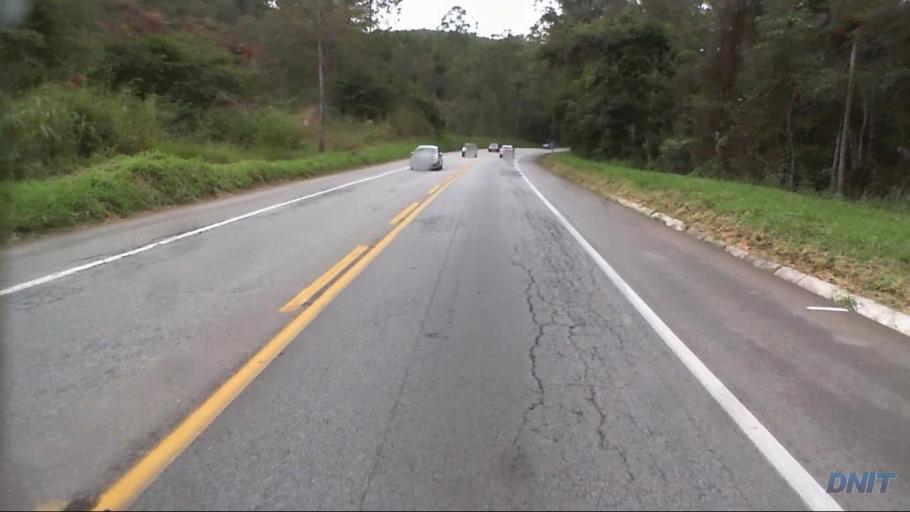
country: BR
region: Minas Gerais
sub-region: Joao Monlevade
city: Joao Monlevade
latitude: -19.8538
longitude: -43.1361
